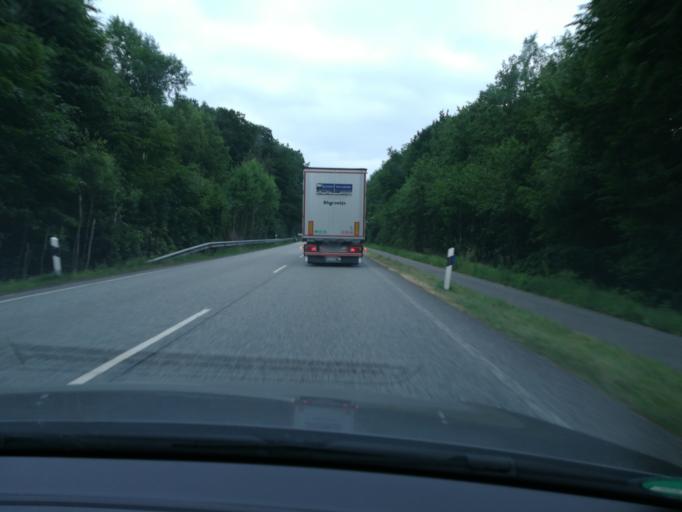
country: DE
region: Schleswig-Holstein
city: Kasseburg
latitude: 53.5412
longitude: 10.4227
